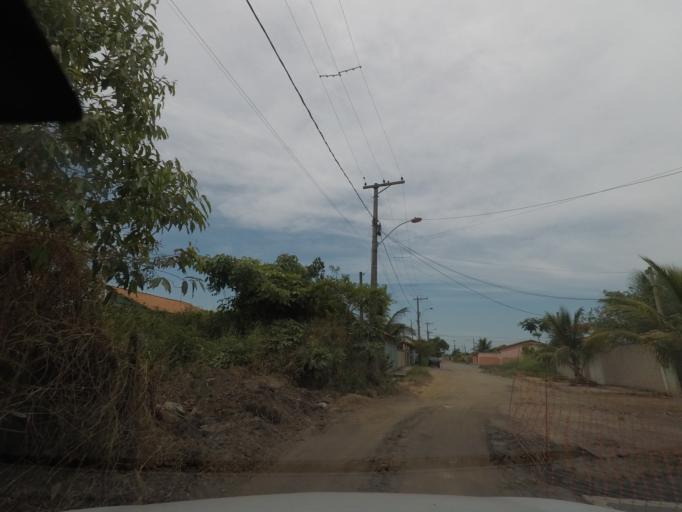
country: BR
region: Rio de Janeiro
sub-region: Marica
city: Marica
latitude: -22.9594
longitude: -42.9513
